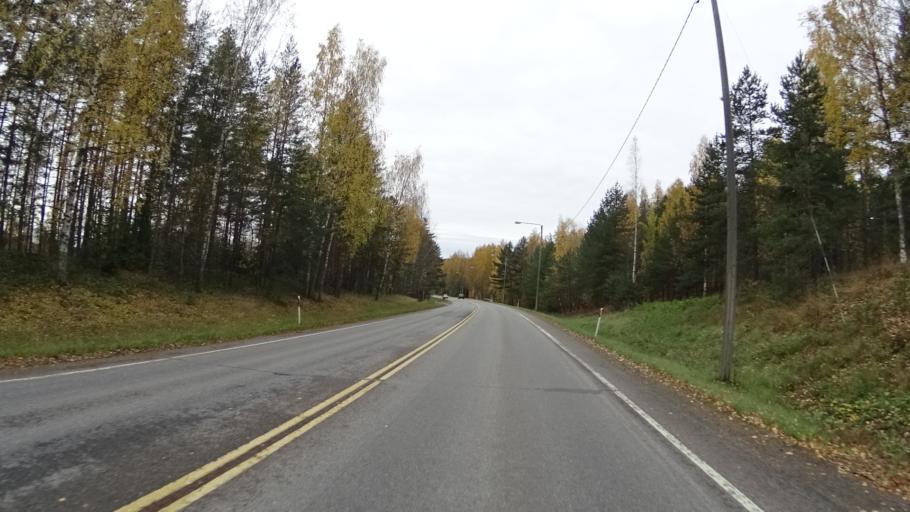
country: FI
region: South Karelia
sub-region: Lappeenranta
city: Lemi
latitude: 60.9551
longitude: 27.7735
